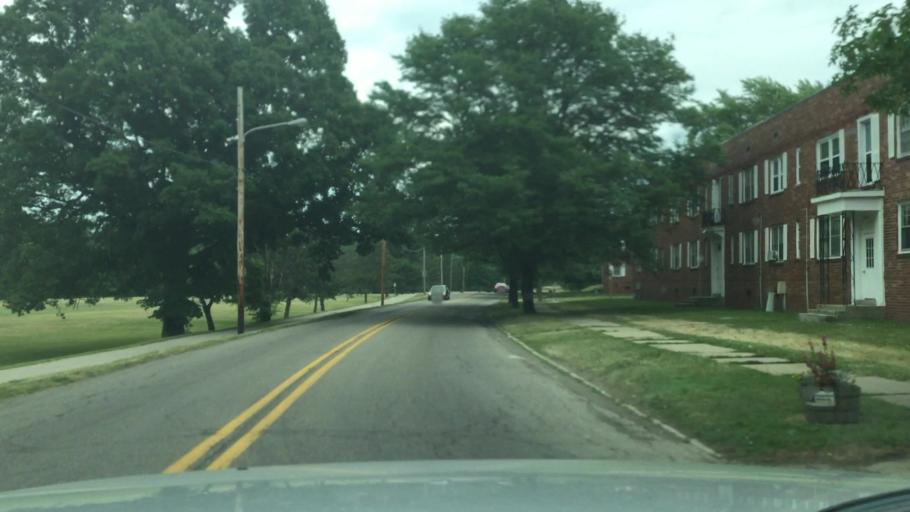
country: US
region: Michigan
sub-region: Genesee County
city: Flint
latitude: 43.0127
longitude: -83.7249
